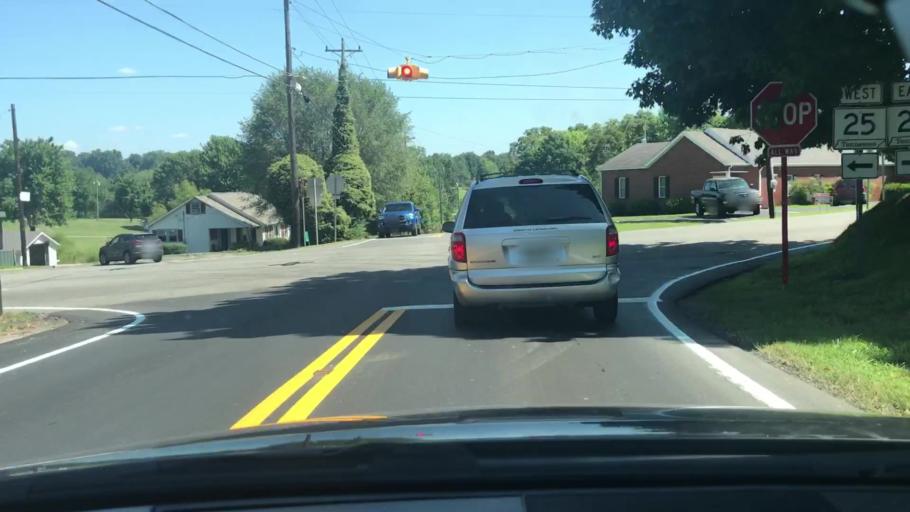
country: US
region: Tennessee
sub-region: Sumner County
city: White House
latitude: 36.4940
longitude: -86.5931
